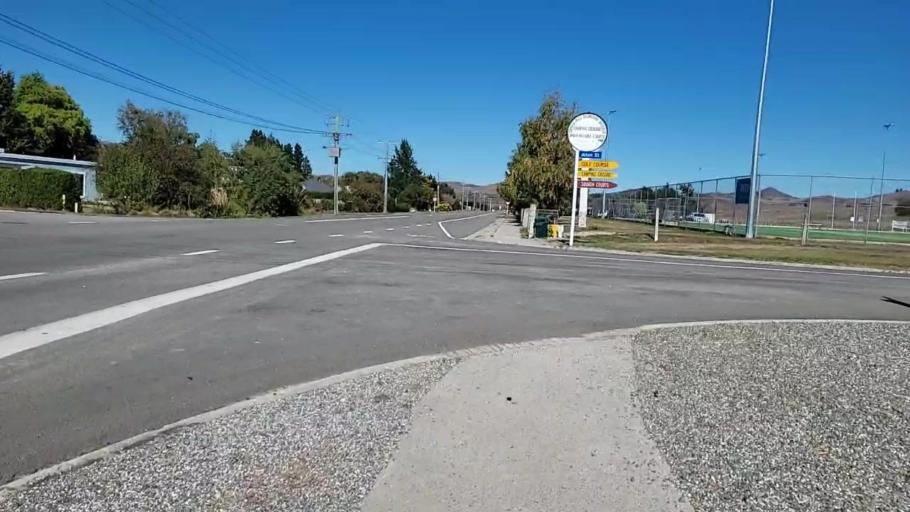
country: NZ
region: Otago
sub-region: Queenstown-Lakes District
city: Wanaka
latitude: -45.0994
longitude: 169.5971
